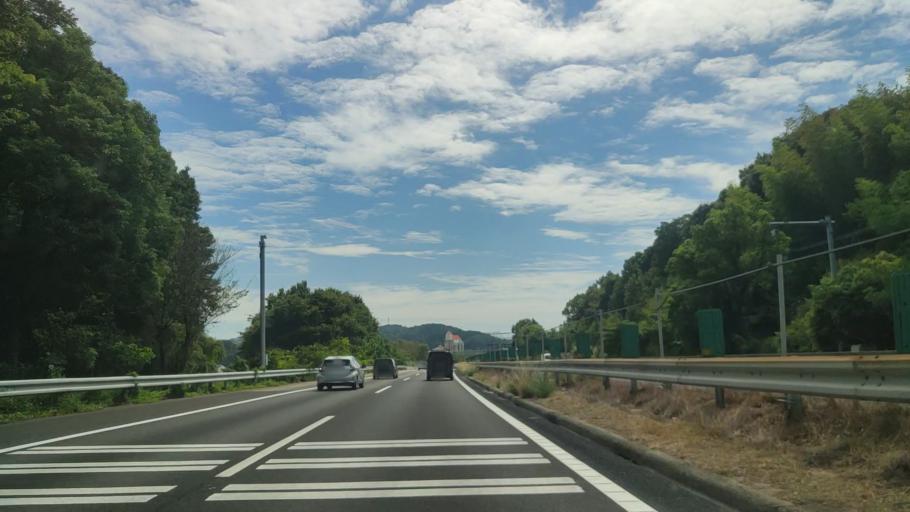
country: JP
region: Aichi
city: Okazaki
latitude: 34.9941
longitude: 137.1832
